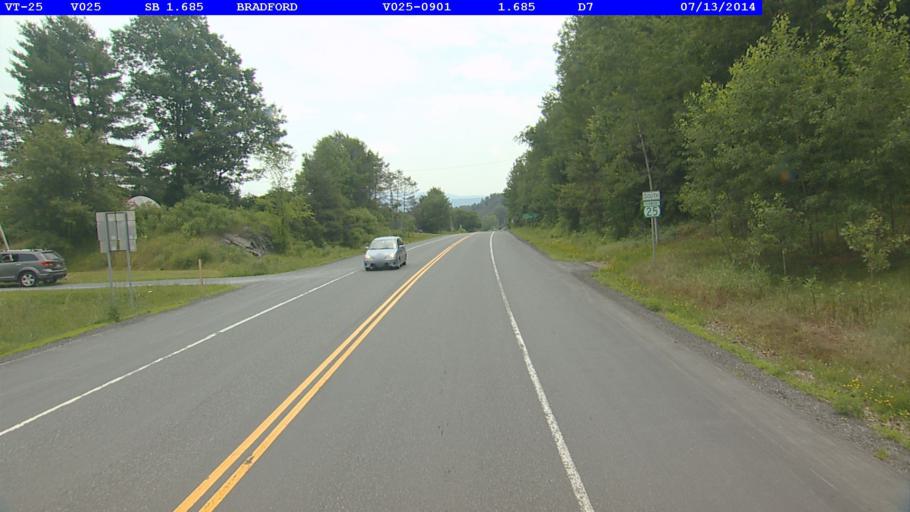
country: US
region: New Hampshire
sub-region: Grafton County
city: Orford
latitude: 43.9862
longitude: -72.1424
